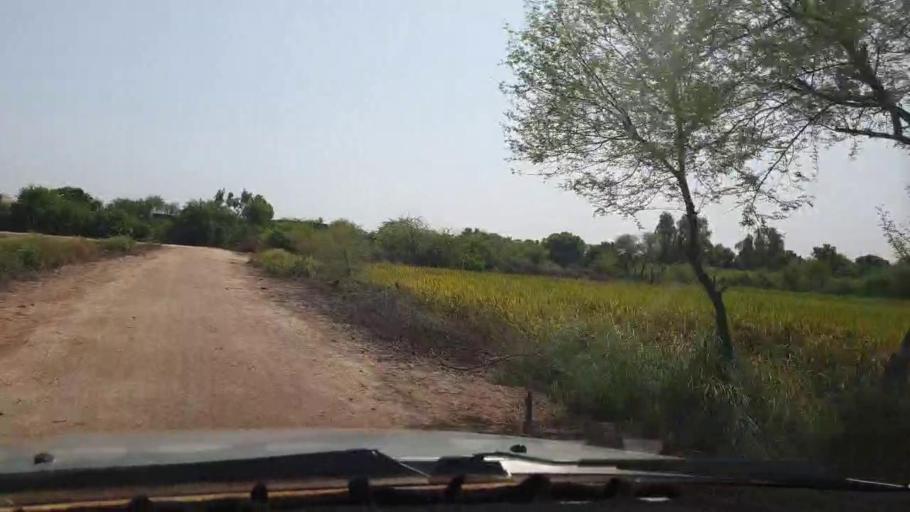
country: PK
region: Sindh
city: Tando Ghulam Ali
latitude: 25.1429
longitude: 68.7753
